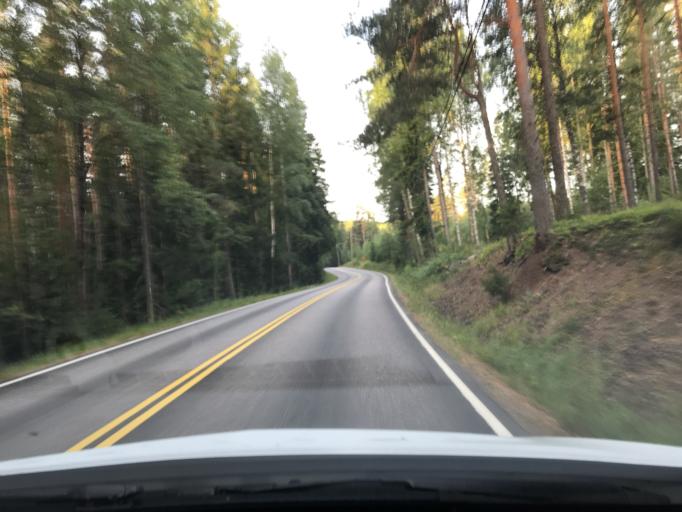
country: FI
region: Uusimaa
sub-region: Helsinki
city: Vihti
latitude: 60.4138
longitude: 24.4727
